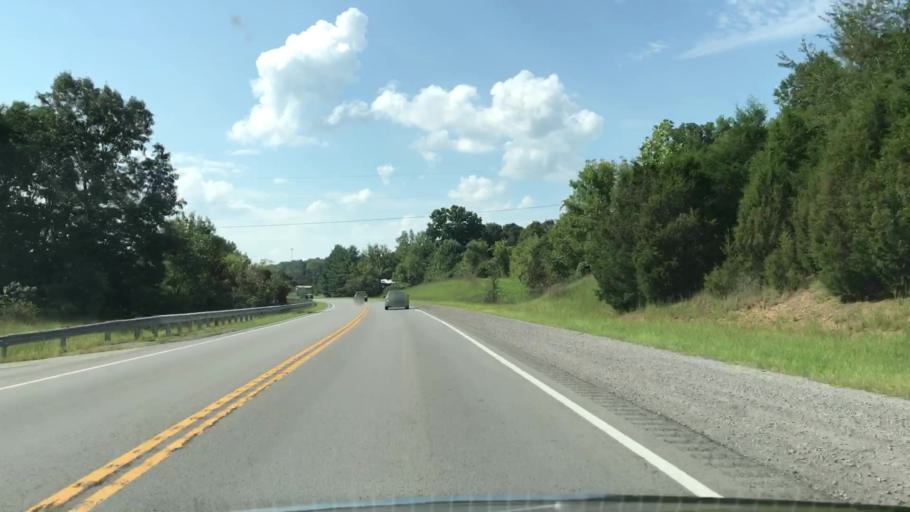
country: US
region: Kentucky
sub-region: Allen County
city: Scottsville
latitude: 36.6875
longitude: -86.2533
